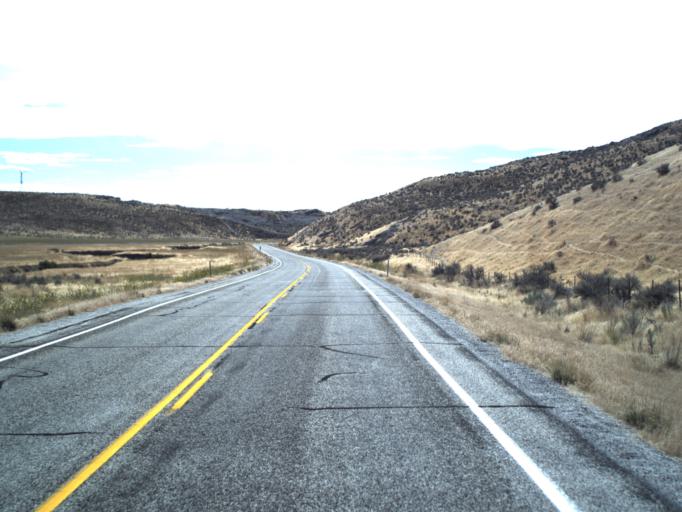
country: US
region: Utah
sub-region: Box Elder County
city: Tremonton
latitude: 41.6835
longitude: -112.4443
